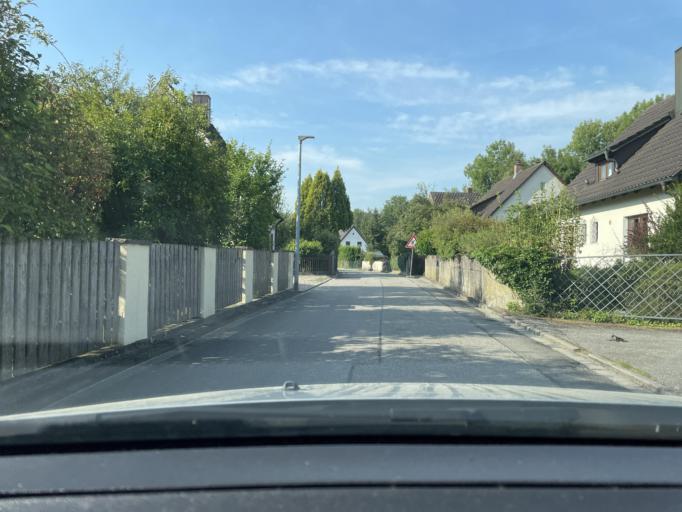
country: DE
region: Bavaria
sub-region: Upper Bavaria
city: Muehldorf
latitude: 48.2363
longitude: 12.5300
